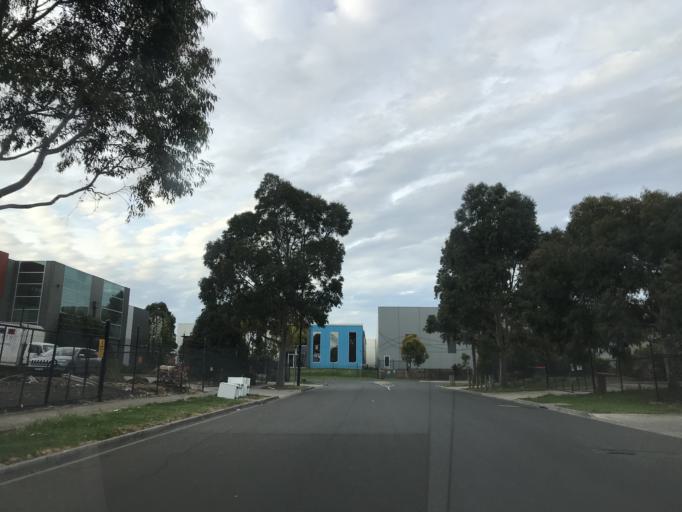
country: AU
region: Victoria
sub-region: Brimbank
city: Derrimut
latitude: -37.8006
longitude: 144.7559
